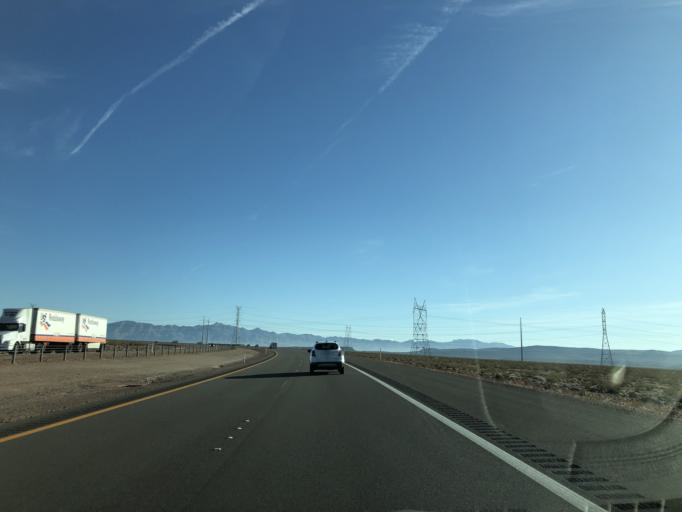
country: US
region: Nevada
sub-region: Clark County
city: Boulder City
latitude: 35.9387
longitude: -114.8182
